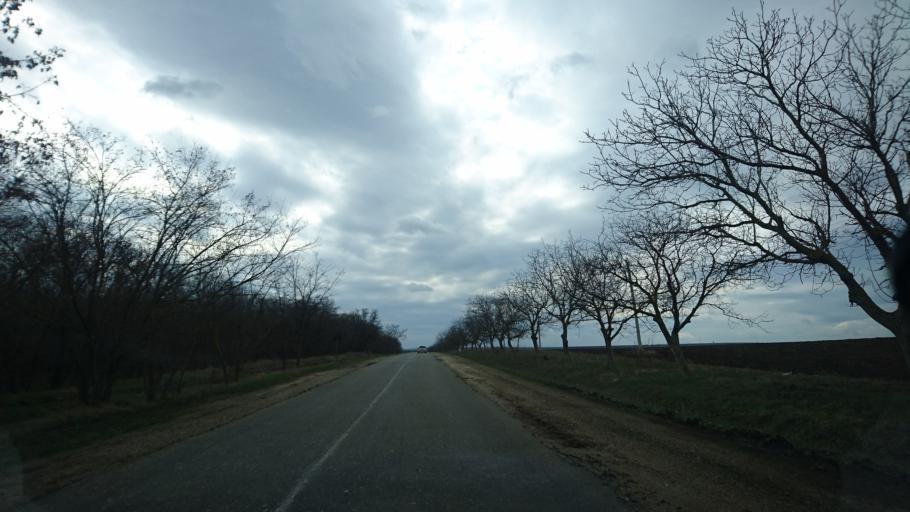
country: MD
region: Cantemir
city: Visniovca
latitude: 46.3222
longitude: 28.5248
